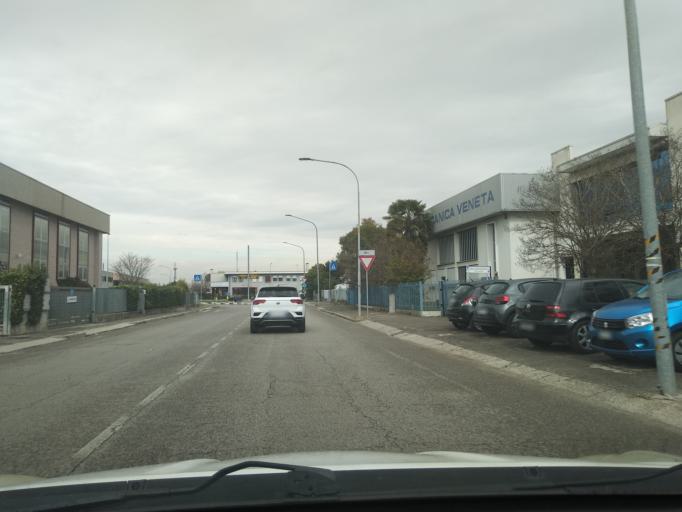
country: IT
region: Veneto
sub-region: Provincia di Padova
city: Rubano
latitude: 45.4178
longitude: 11.7939
